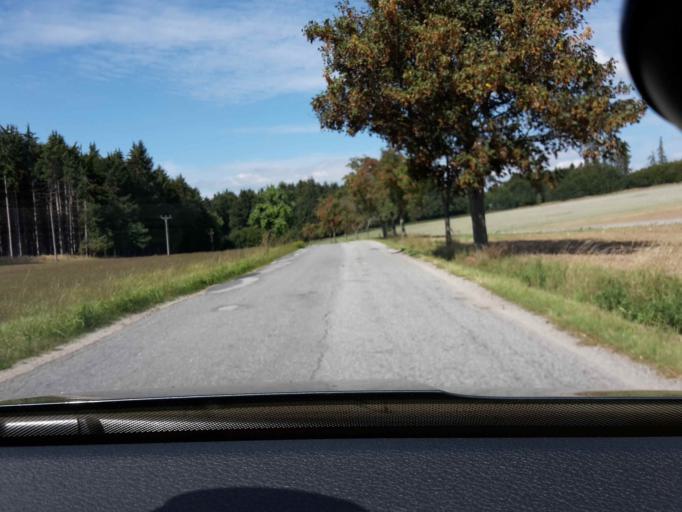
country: CZ
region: Vysocina
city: Zeletava
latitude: 49.1272
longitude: 15.6040
